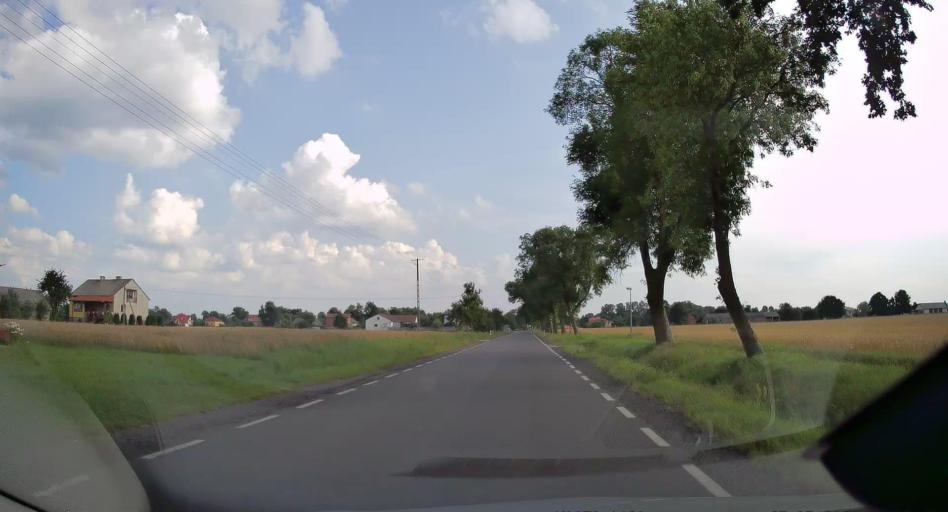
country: PL
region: Lodz Voivodeship
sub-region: Powiat tomaszowski
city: Rzeczyca
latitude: 51.6039
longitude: 20.2936
